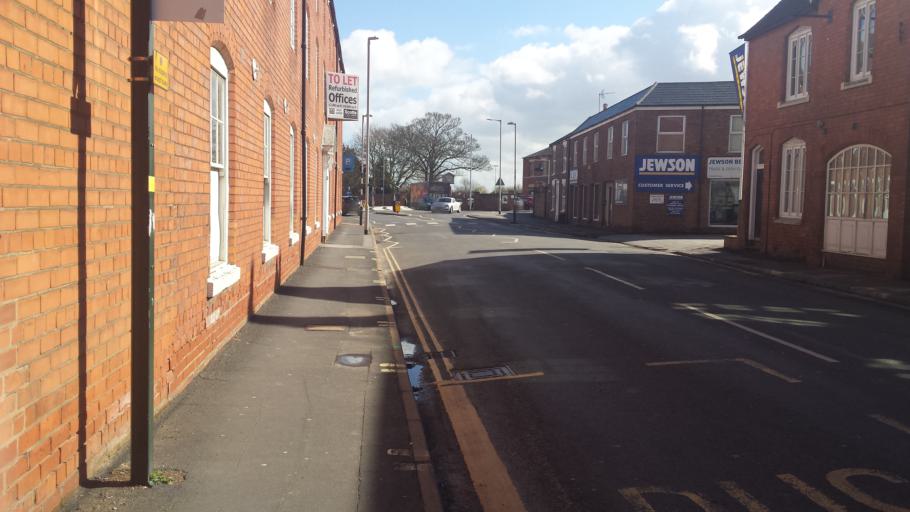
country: GB
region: England
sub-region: East Riding of Yorkshire
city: Beverley
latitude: 53.8389
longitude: -0.4210
